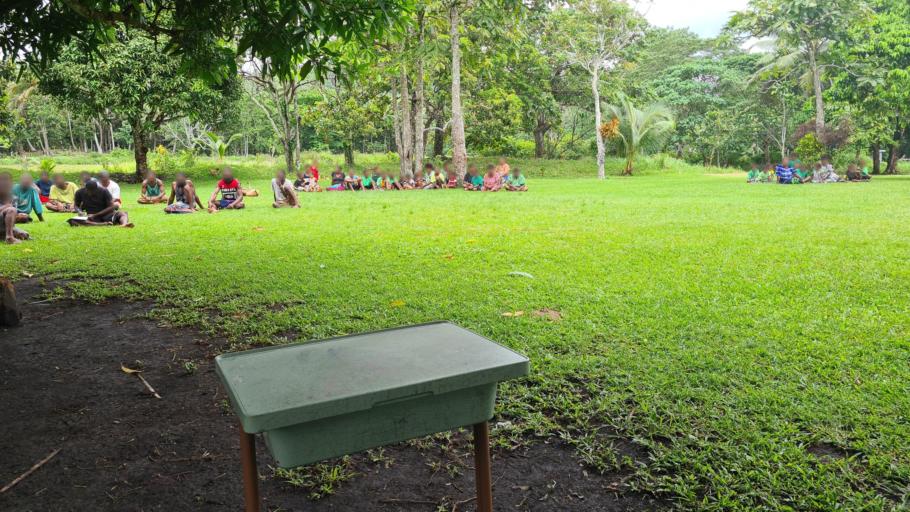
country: VU
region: Malampa
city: Lakatoro
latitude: -16.3083
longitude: 168.2882
